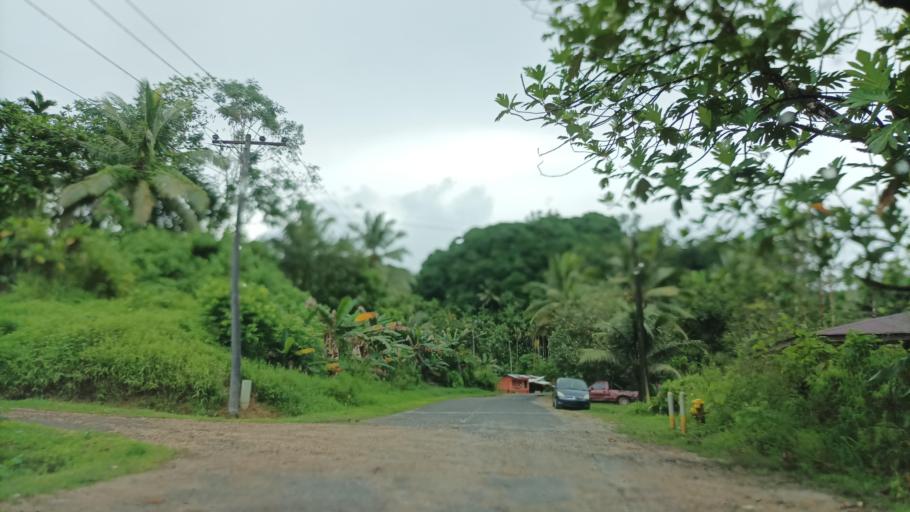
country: FM
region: Pohnpei
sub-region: Sokehs Municipality
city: Palikir - National Government Center
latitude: 6.8306
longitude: 158.1565
